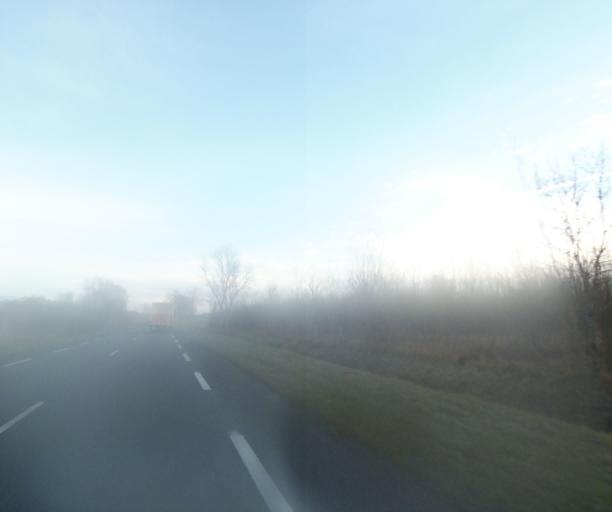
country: FR
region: Poitou-Charentes
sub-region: Departement de la Charente-Maritime
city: Fontcouverte
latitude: 45.7731
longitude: -0.5761
